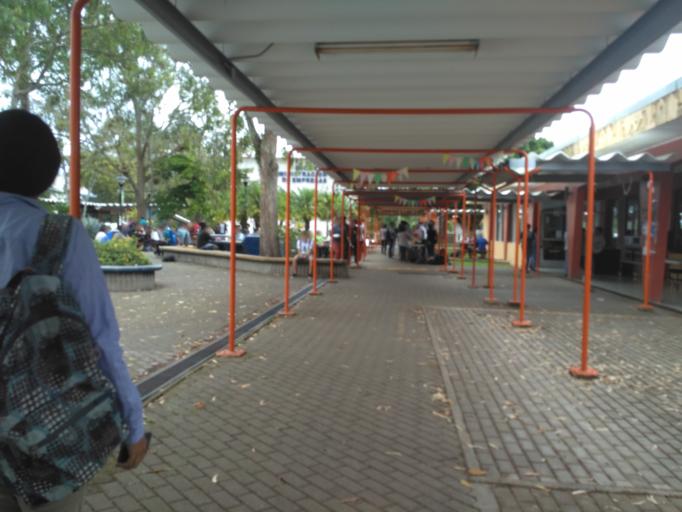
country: CR
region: Cartago
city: Cartago
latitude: 9.8556
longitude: -83.9131
